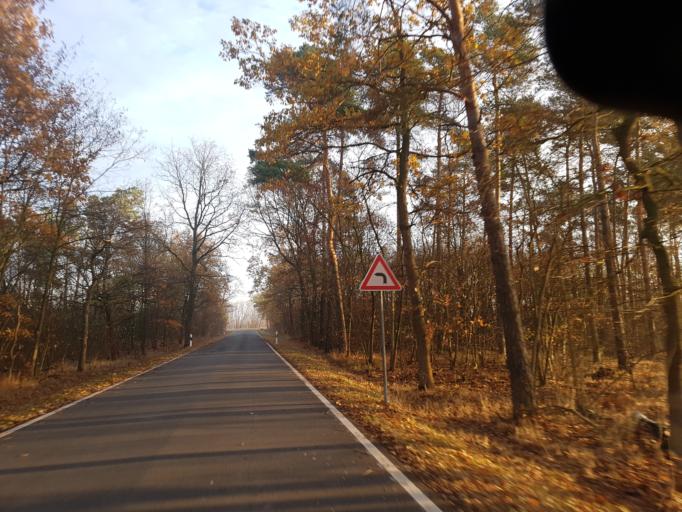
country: DE
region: Saxony-Anhalt
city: Elster
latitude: 51.8528
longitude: 12.8433
